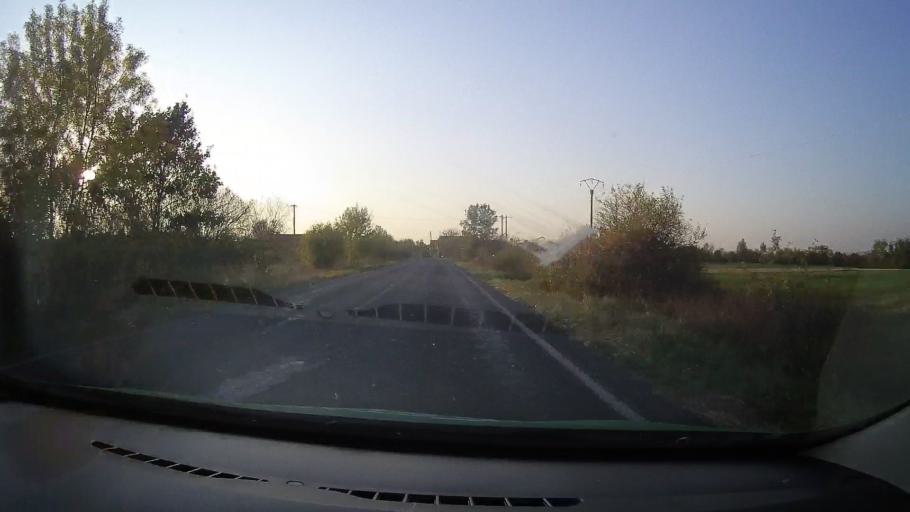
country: RO
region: Arad
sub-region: Comuna Barsa
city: Barsa
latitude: 46.3929
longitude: 22.0471
